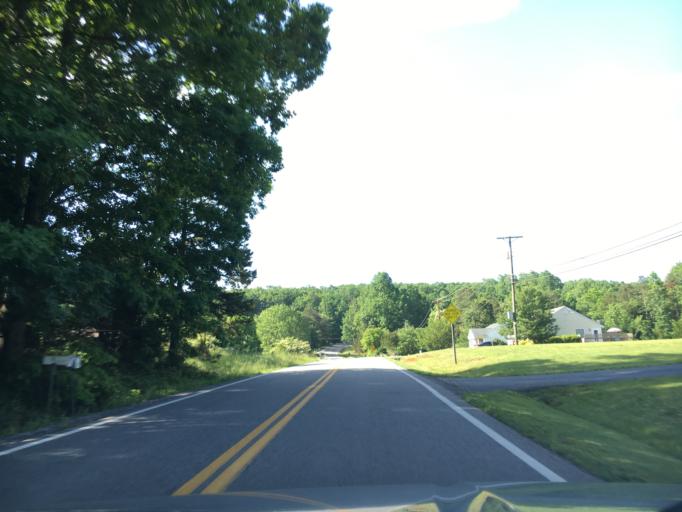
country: US
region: Virginia
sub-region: Campbell County
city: Rustburg
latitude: 37.3113
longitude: -79.1564
